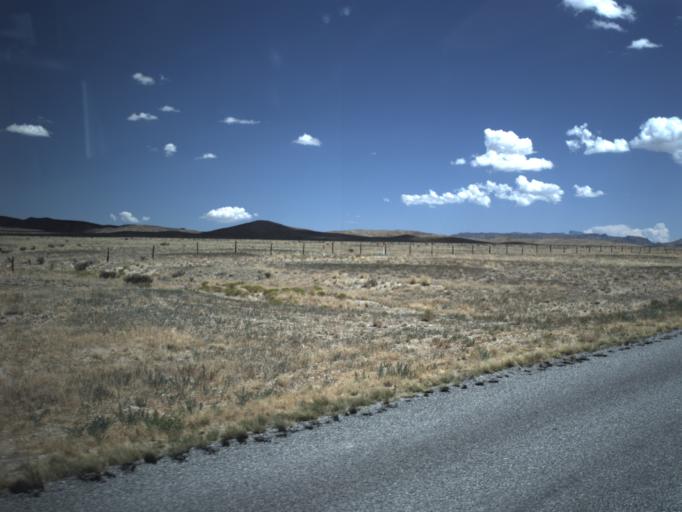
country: US
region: Nevada
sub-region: White Pine County
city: McGill
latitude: 39.0406
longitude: -113.8346
